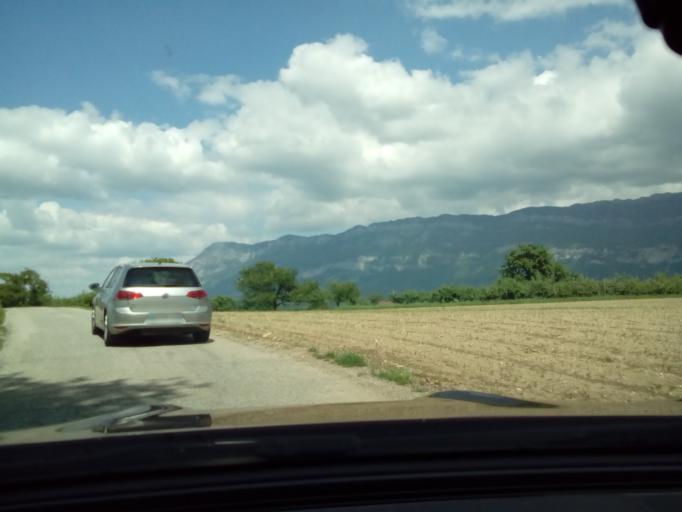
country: FR
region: Rhone-Alpes
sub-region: Departement de la Savoie
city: La Motte-Servolex
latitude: 45.6160
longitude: 5.8626
